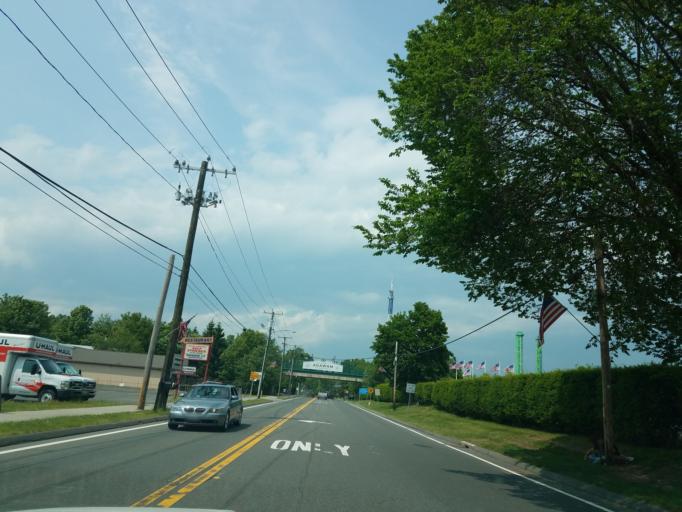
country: US
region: Massachusetts
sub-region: Hampden County
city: Agawam
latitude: 42.0365
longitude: -72.6166
